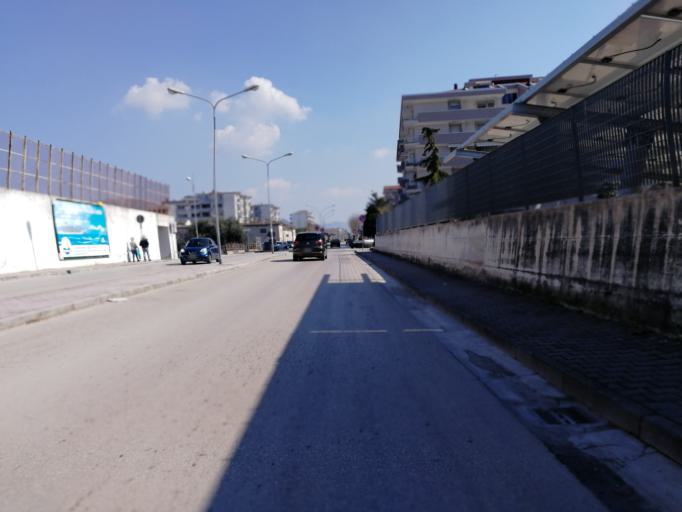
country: IT
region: Campania
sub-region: Provincia di Caserta
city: Santa Maria Capua Vetere
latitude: 41.0877
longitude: 14.2568
